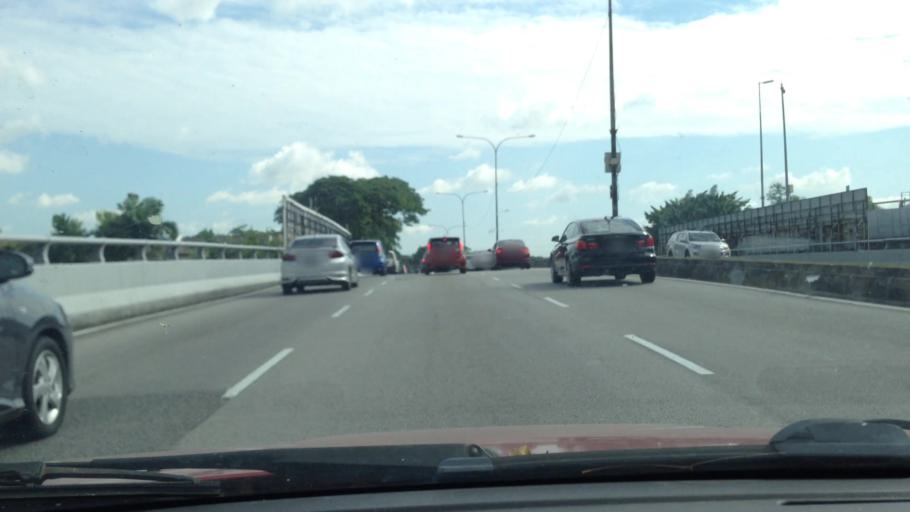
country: MY
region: Selangor
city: Subang Jaya
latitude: 3.0626
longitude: 101.5803
